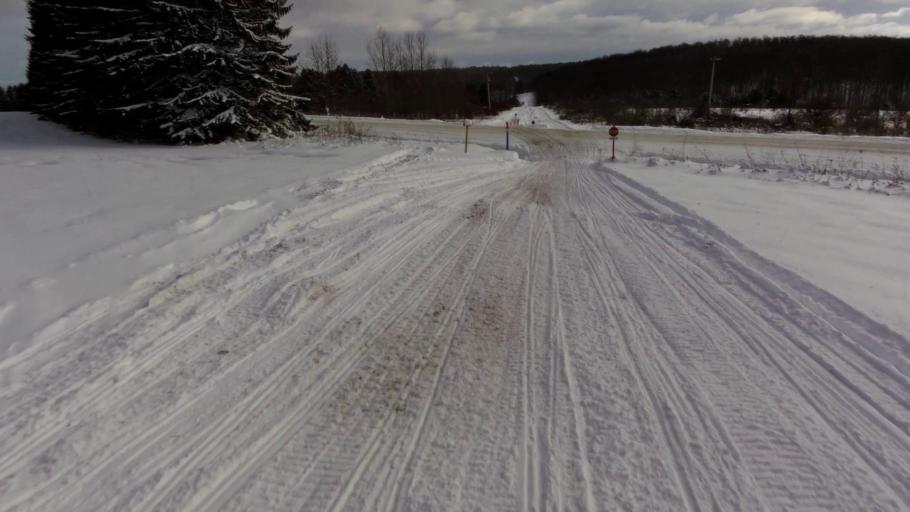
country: US
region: New York
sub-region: Cattaraugus County
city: Franklinville
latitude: 42.3152
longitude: -78.5379
